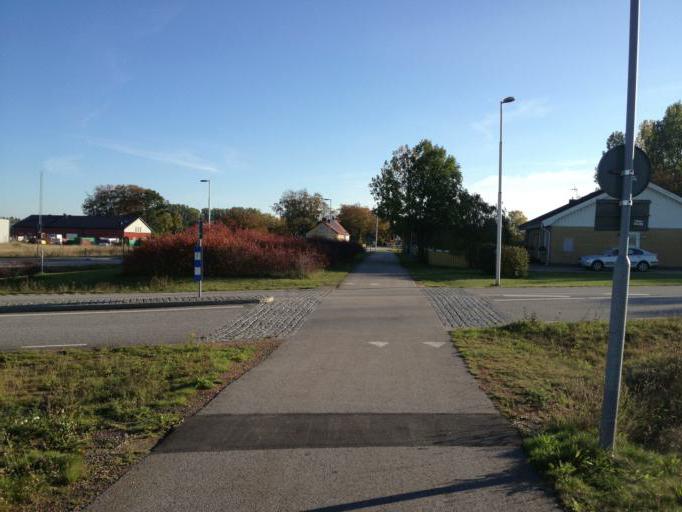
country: SE
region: Skane
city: Bjarred
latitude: 55.7407
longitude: 13.0307
